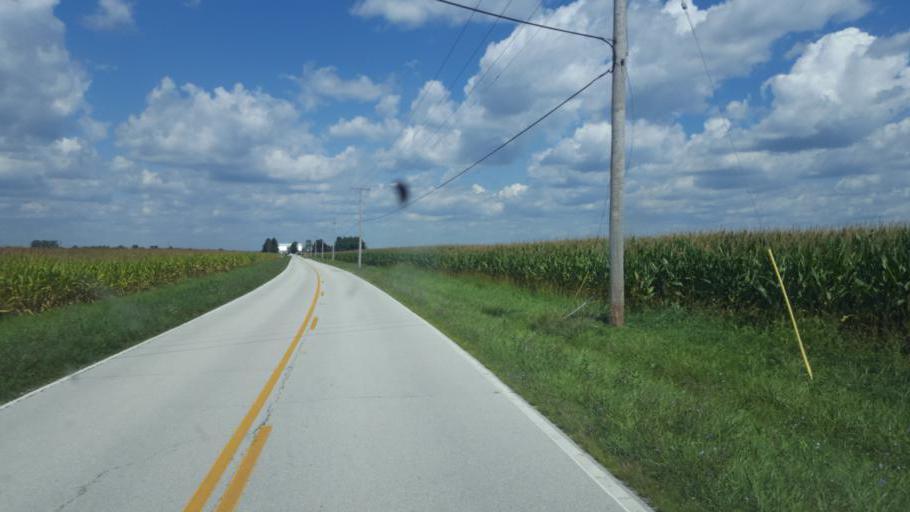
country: US
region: Ohio
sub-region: Sandusky County
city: Gibsonburg
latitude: 41.3359
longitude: -83.3056
